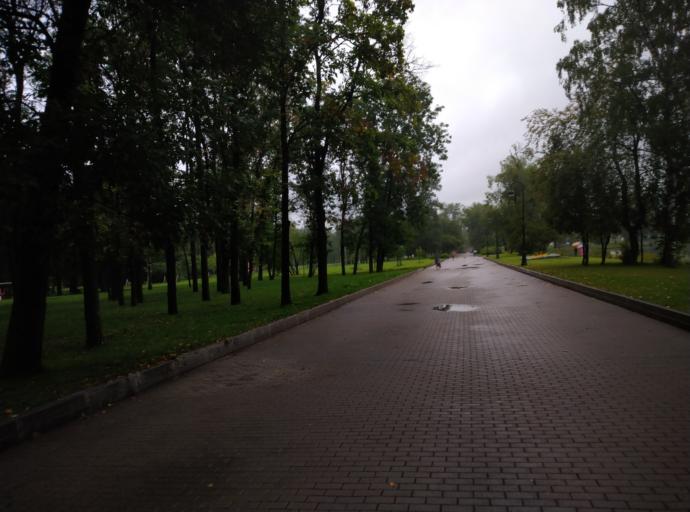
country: RU
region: St.-Petersburg
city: Kupchino
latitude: 59.8676
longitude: 30.3276
